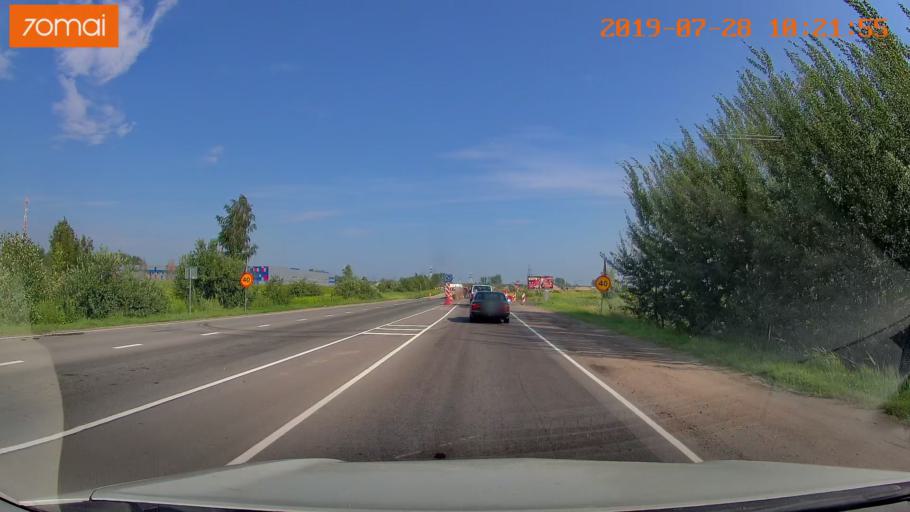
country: RU
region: Kaliningrad
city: Maloye Isakovo
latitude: 54.7597
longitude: 20.5632
